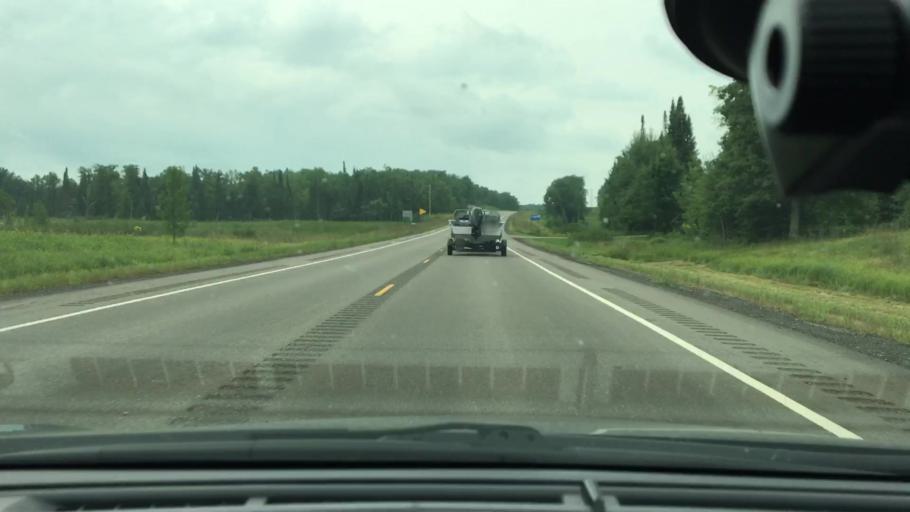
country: US
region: Minnesota
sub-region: Crow Wing County
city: Crosby
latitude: 46.6244
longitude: -93.9464
